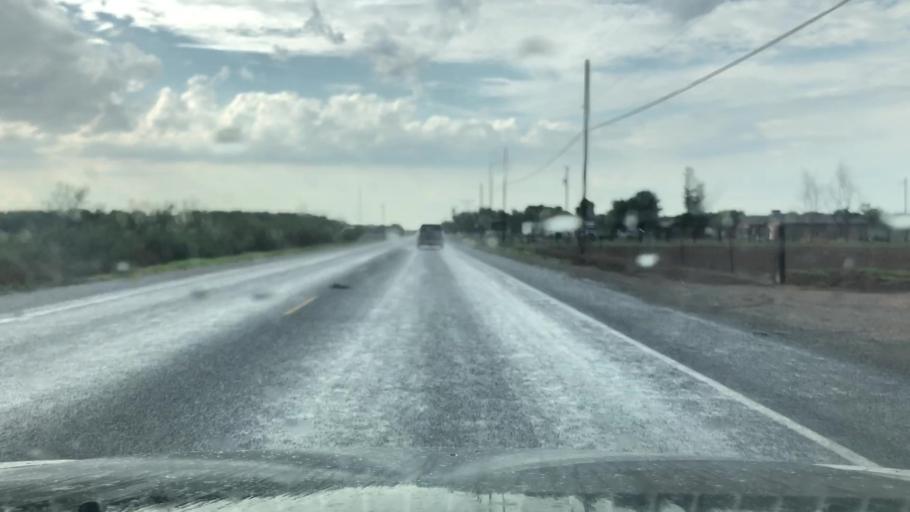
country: US
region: New Mexico
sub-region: Dona Ana County
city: Mesquite
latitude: 32.1900
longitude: -106.7127
